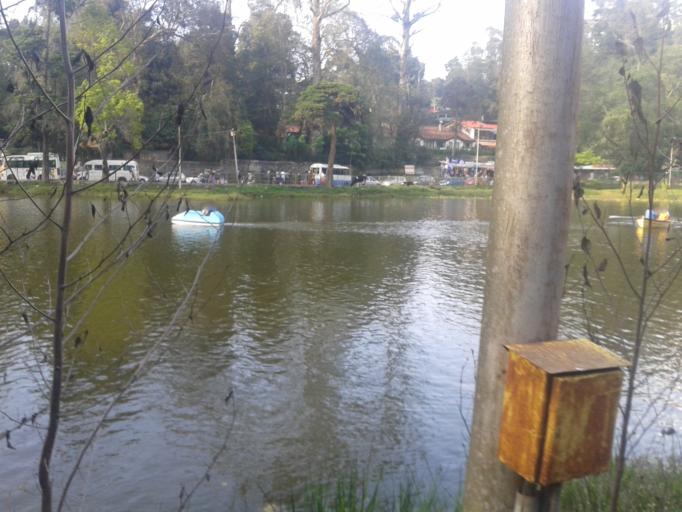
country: IN
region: Tamil Nadu
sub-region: Dindigul
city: Kodaikanal
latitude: 10.2322
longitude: 77.4906
